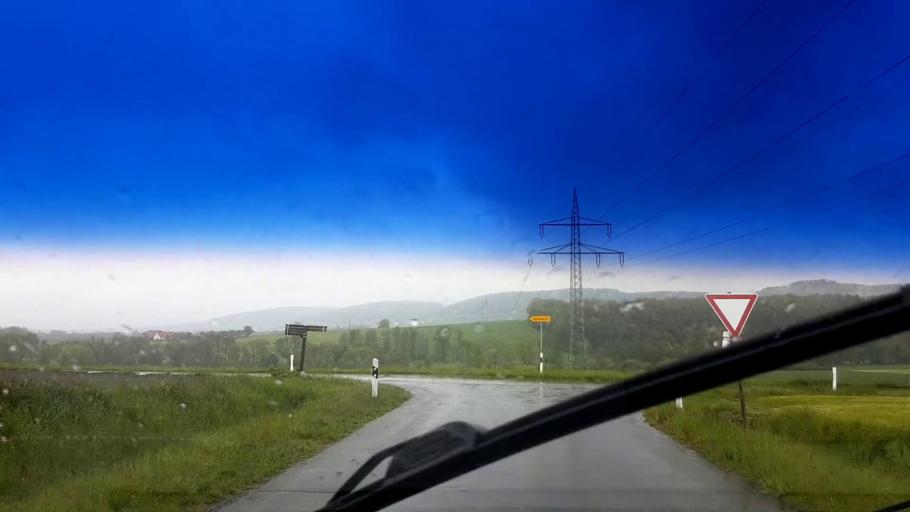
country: DE
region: Bavaria
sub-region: Upper Franconia
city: Gesees
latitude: 50.0292
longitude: 11.6282
